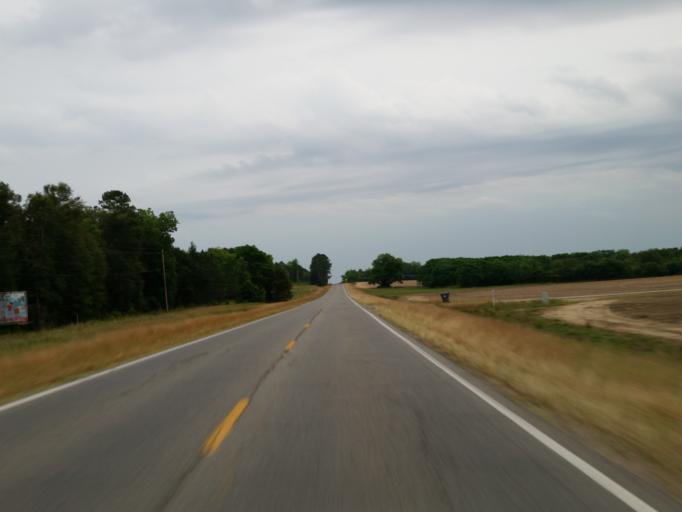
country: US
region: Georgia
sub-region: Crisp County
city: Cordele
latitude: 32.0167
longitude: -83.7916
